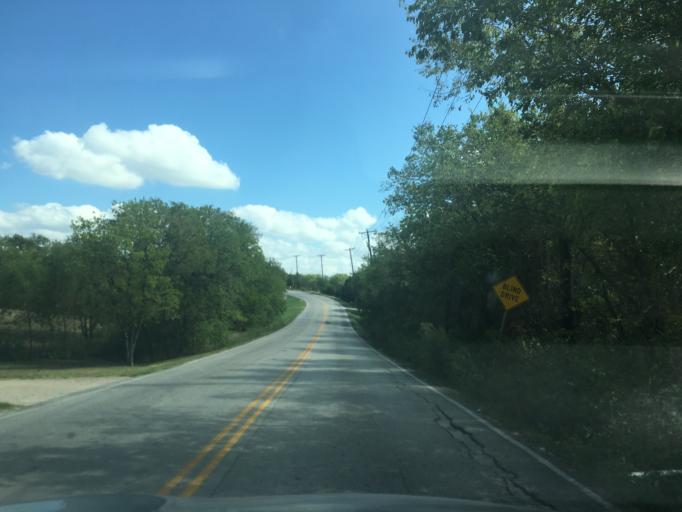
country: US
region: Texas
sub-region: Dallas County
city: Sachse
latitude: 32.9530
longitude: -96.5686
